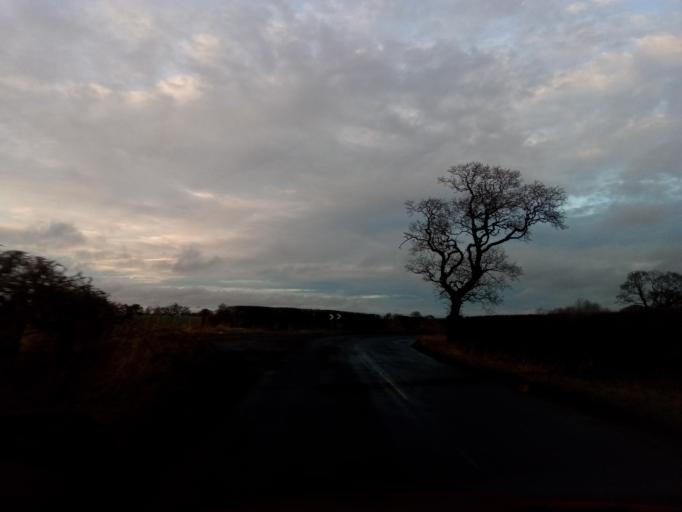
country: GB
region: England
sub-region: Northumberland
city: Ponteland
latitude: 55.0960
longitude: -1.7529
